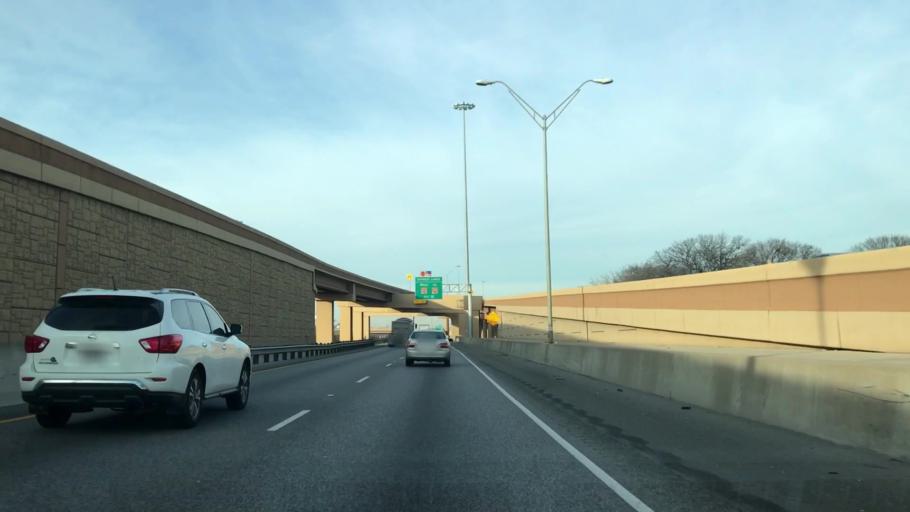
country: US
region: Texas
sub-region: Tarrant County
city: Watauga
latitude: 32.8402
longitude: -97.2582
